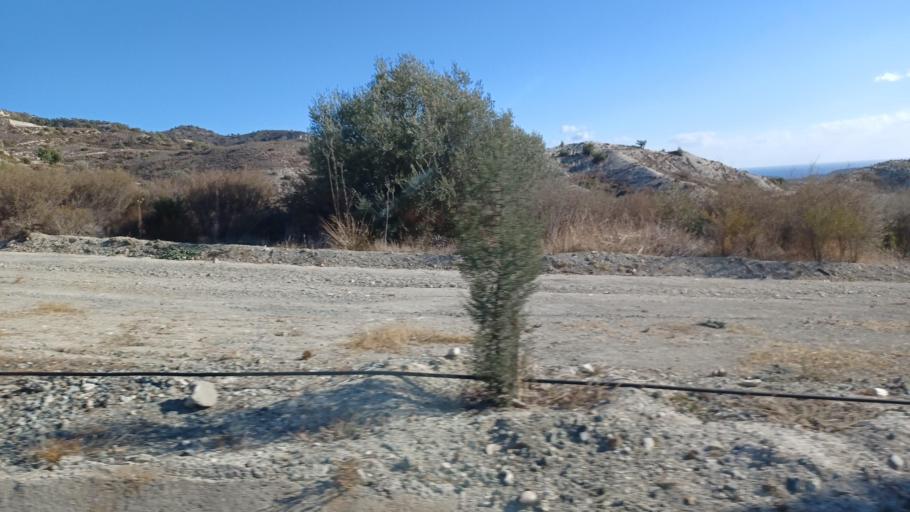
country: CY
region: Limassol
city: Pyrgos
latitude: 34.7646
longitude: 33.2303
